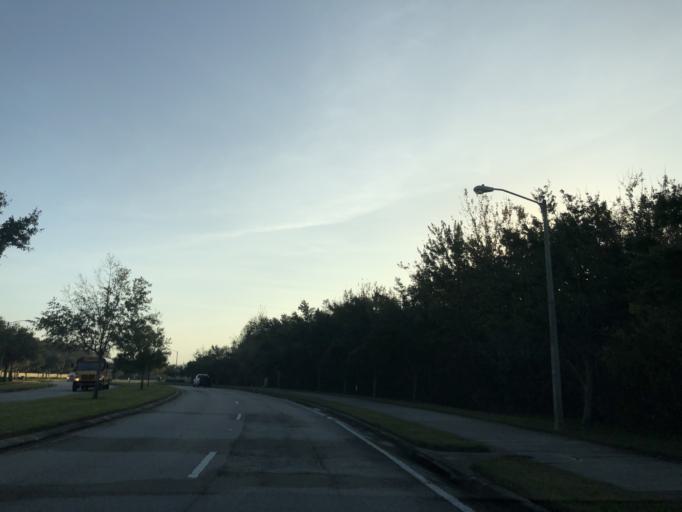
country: US
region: Florida
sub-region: Osceola County
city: Kissimmee
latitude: 28.3307
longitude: -81.4282
